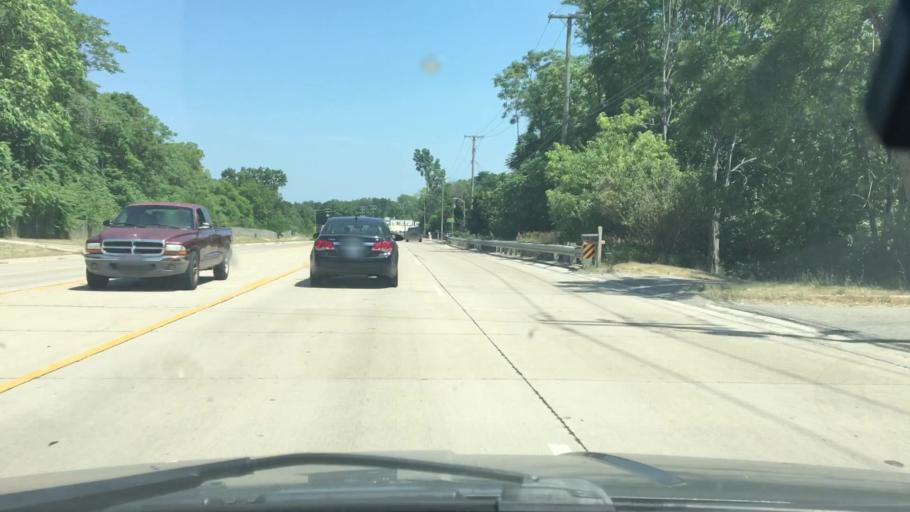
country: US
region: Michigan
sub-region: Livingston County
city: Brighton
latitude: 42.5171
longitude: -83.7419
